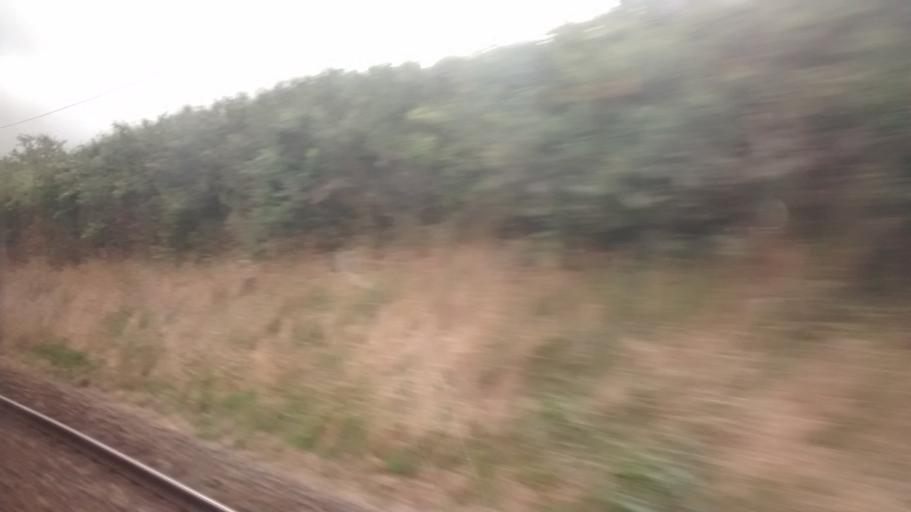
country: FR
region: Pays de la Loire
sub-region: Departement de la Mayenne
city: Louverne
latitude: 48.1199
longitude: -0.6921
